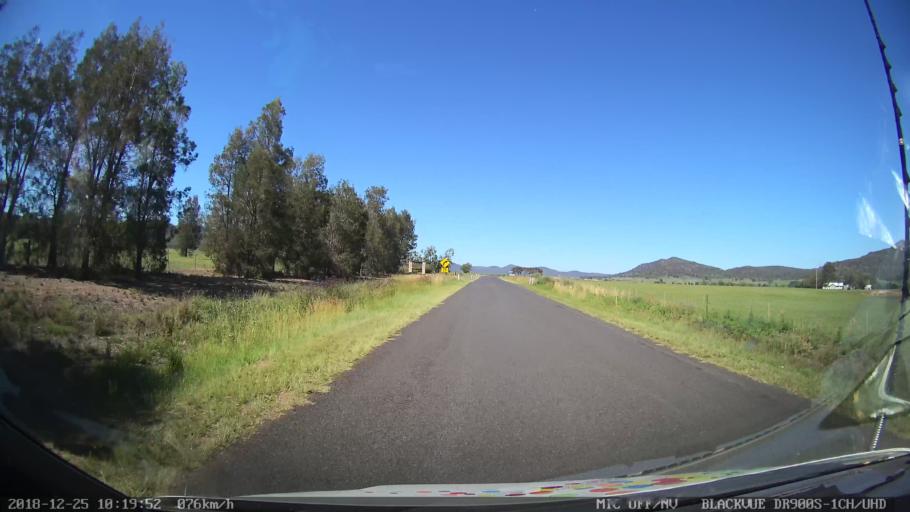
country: AU
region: New South Wales
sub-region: Muswellbrook
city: Denman
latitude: -32.3546
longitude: 150.5550
